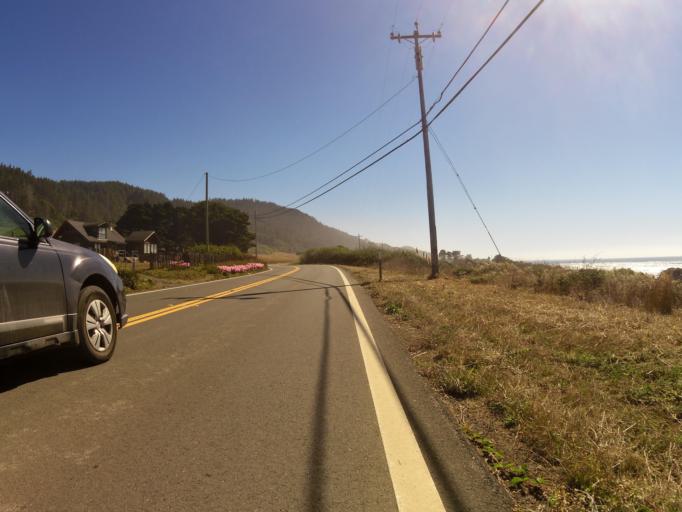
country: US
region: California
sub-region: Mendocino County
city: Fort Bragg
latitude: 39.6453
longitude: -123.7843
